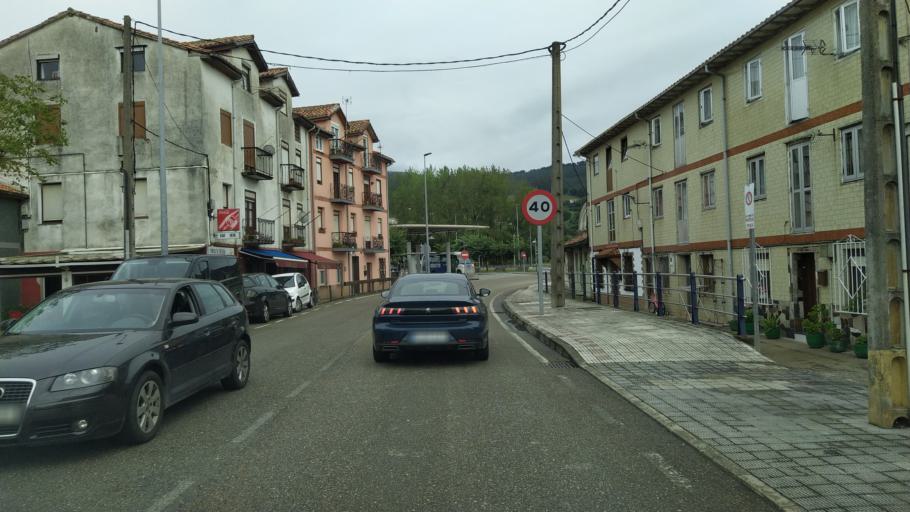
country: ES
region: Cantabria
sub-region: Provincia de Cantabria
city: El Astillero
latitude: 43.3952
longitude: -3.8163
